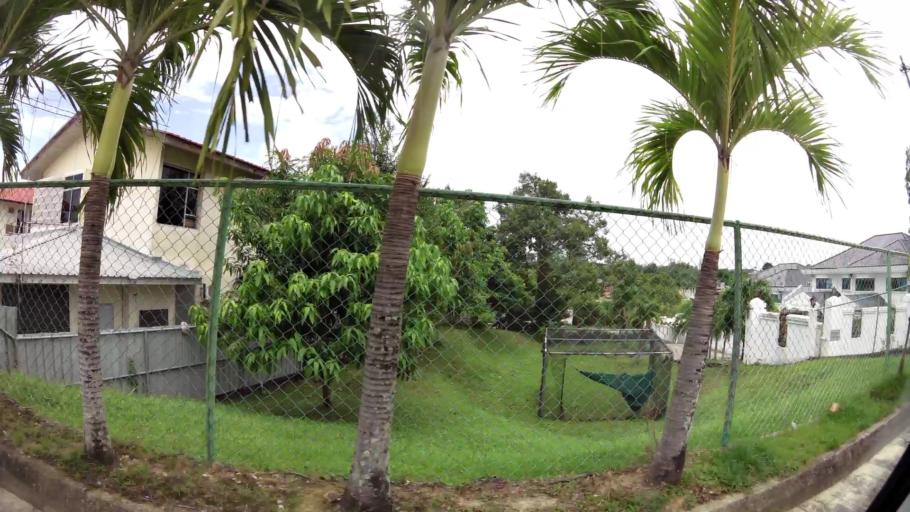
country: BN
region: Brunei and Muara
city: Bandar Seri Begawan
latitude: 4.9134
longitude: 114.9188
